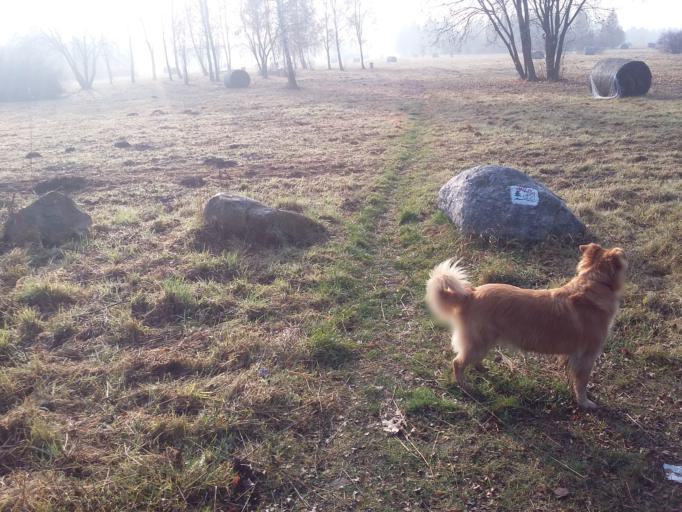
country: PL
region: Lodz Voivodeship
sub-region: Powiat pabianicki
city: Ksawerow
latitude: 51.7348
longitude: 19.3884
